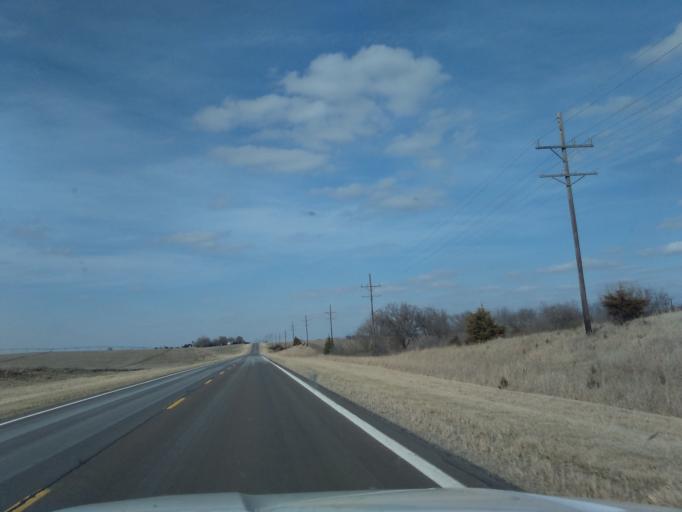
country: US
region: Nebraska
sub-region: Gage County
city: Beatrice
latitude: 40.1405
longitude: -96.9353
